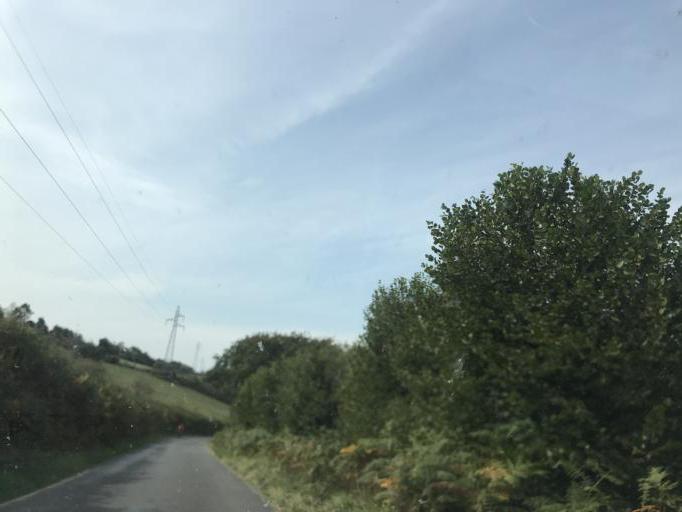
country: FR
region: Brittany
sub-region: Departement du Finistere
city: Brasparts
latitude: 48.3345
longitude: -3.9014
